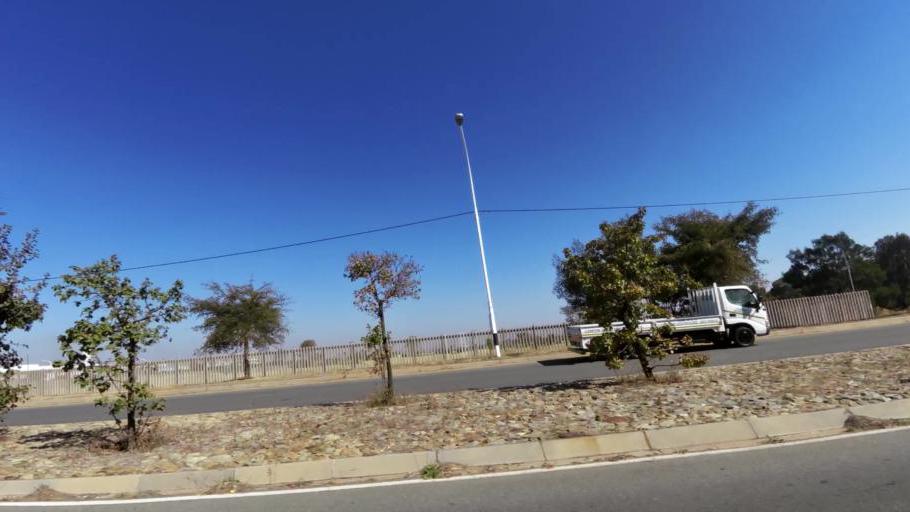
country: ZA
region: Gauteng
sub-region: City of Johannesburg Metropolitan Municipality
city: Johannesburg
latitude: -26.2473
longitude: 27.9758
